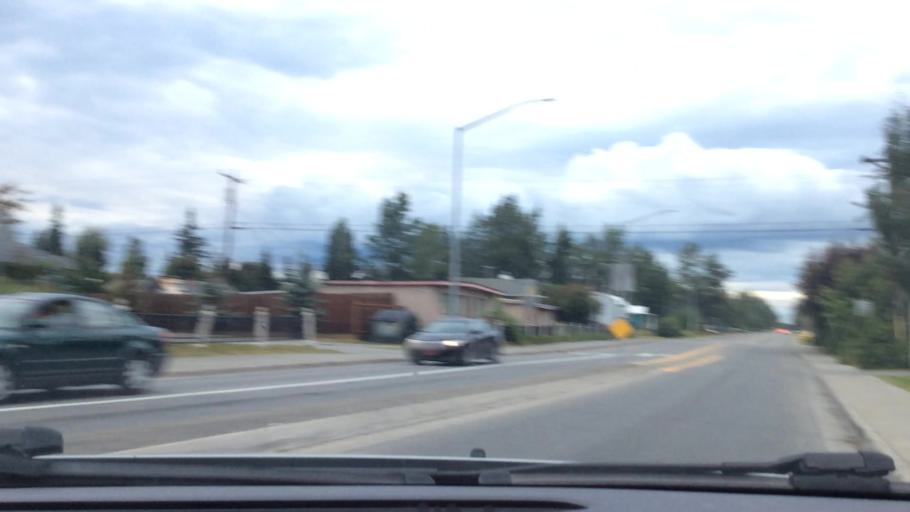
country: US
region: Alaska
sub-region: Anchorage Municipality
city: Elmendorf Air Force Base
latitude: 61.2099
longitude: -149.7559
